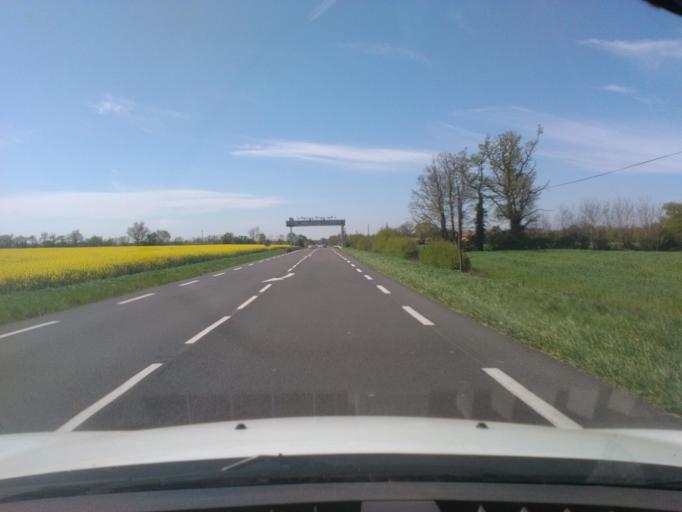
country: FR
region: Rhone-Alpes
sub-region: Departement de l'Ain
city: Saint-Paul-de-Varax
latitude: 46.0588
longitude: 5.0791
